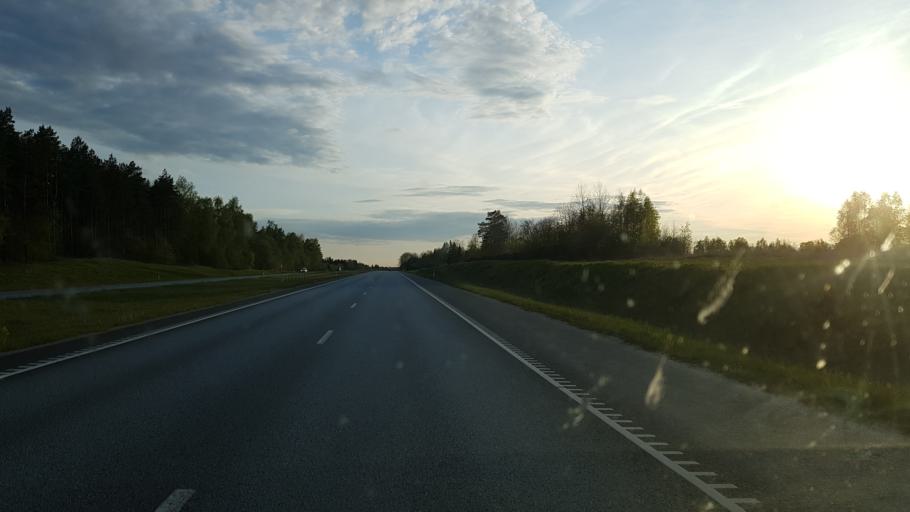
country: EE
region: Harju
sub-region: Raasiku vald
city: Raasiku
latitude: 59.4369
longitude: 25.2262
